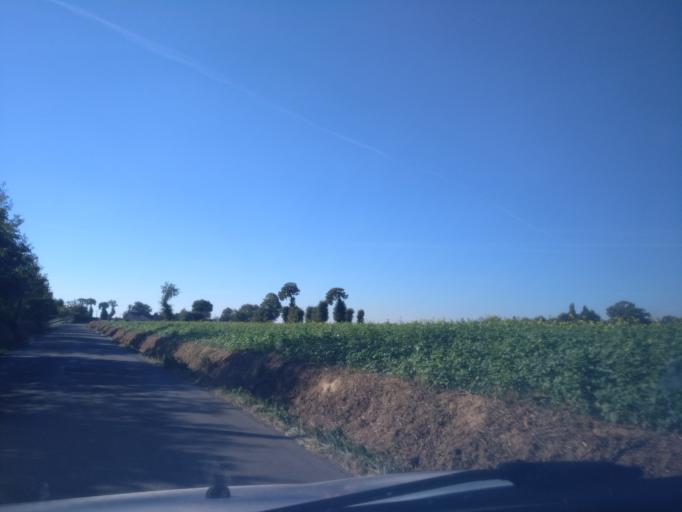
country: FR
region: Brittany
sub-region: Departement d'Ille-et-Vilaine
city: Melesse
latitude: 48.2139
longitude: -1.6751
